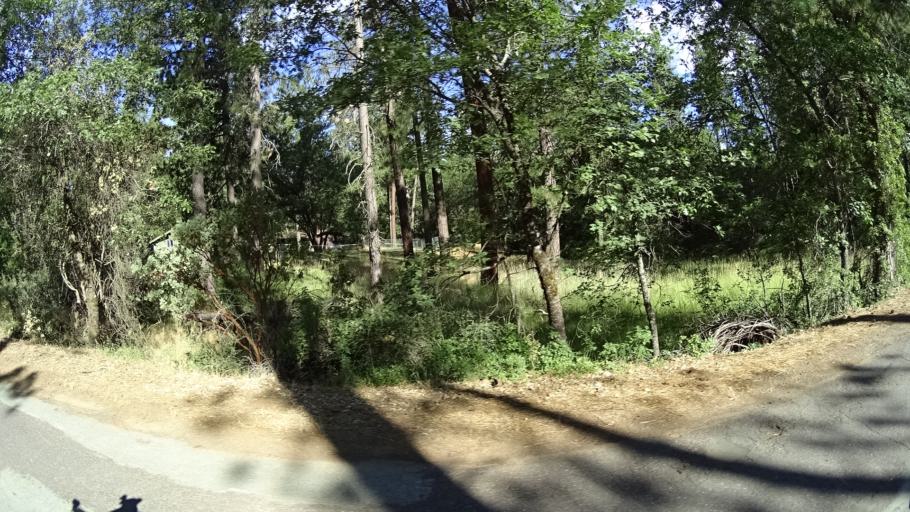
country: US
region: California
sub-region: Amador County
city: Pioneer
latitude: 38.3788
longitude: -120.4510
